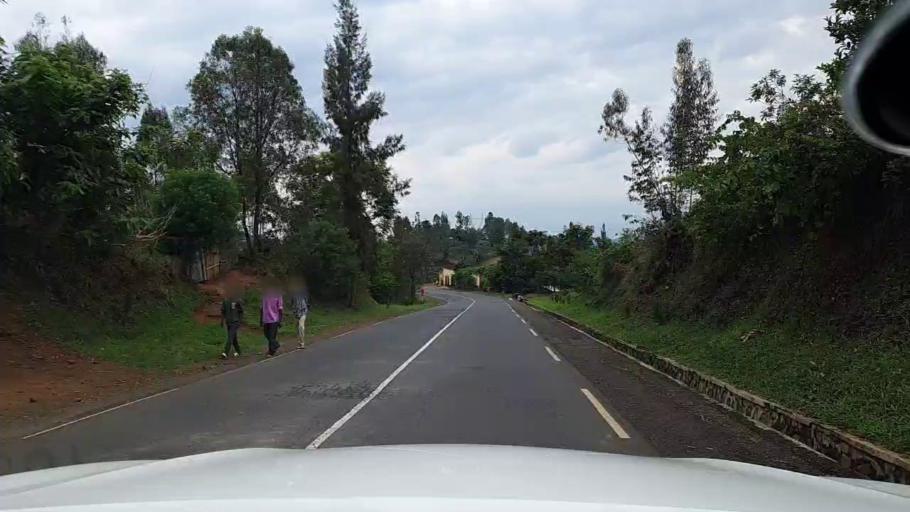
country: RW
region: Western Province
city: Cyangugu
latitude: -2.6609
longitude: 28.9796
